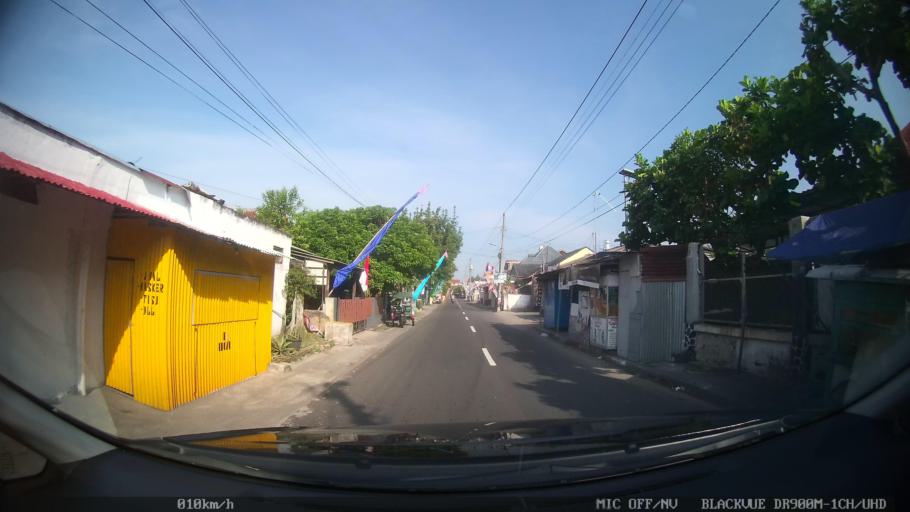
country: ID
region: Daerah Istimewa Yogyakarta
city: Yogyakarta
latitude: -7.7871
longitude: 110.3622
